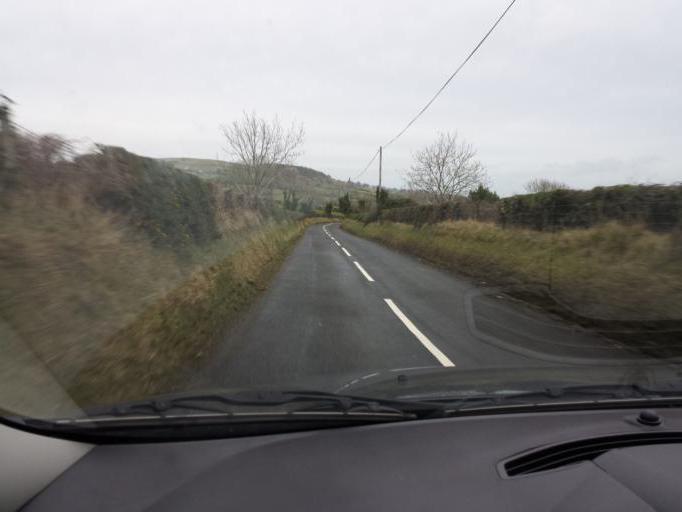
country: GB
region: Northern Ireland
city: Cushendall
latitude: 55.0788
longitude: -6.0901
